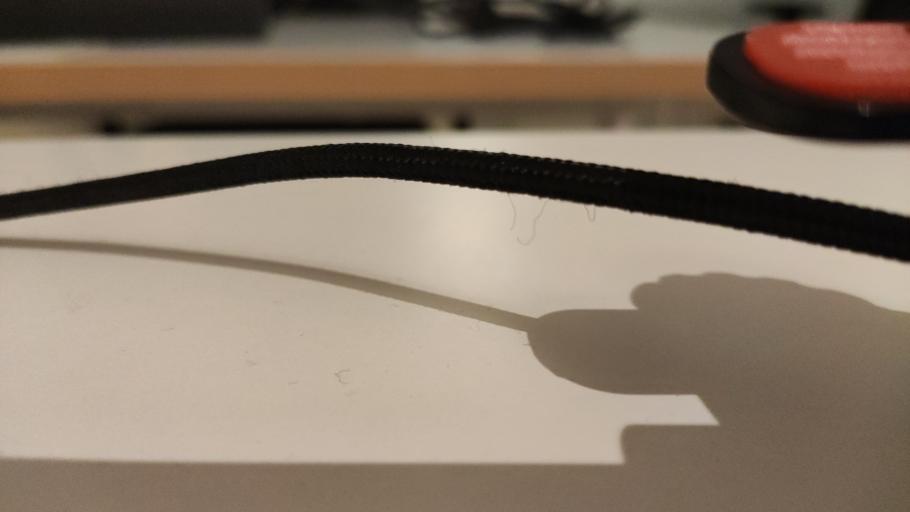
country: RU
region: Moskovskaya
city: Malino
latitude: 55.1236
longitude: 38.2273
